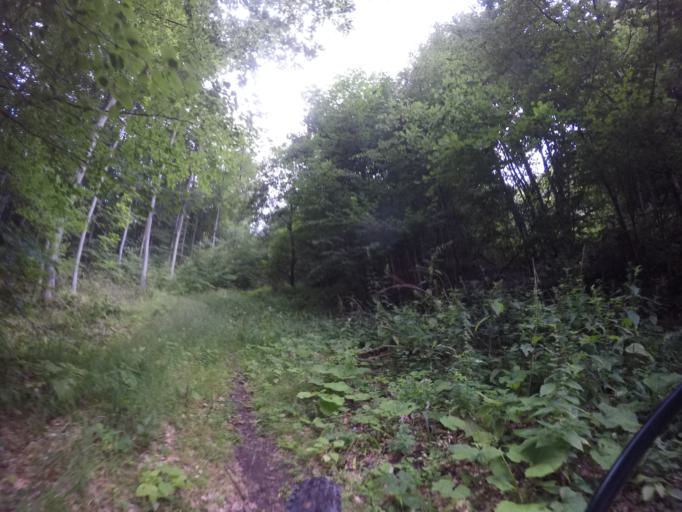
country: SK
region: Kosicky
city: Gelnica
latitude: 48.9259
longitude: 21.0234
